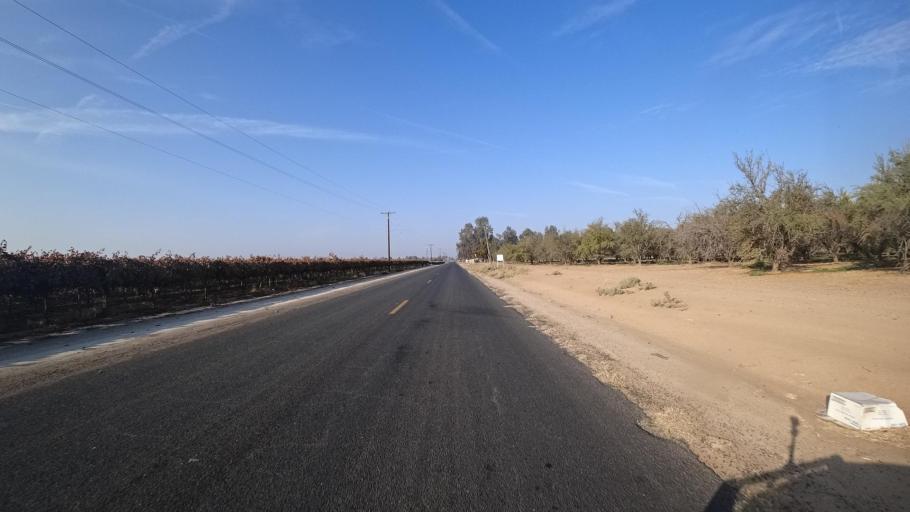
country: US
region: California
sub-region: Kern County
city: McFarland
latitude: 35.6746
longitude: -119.2117
